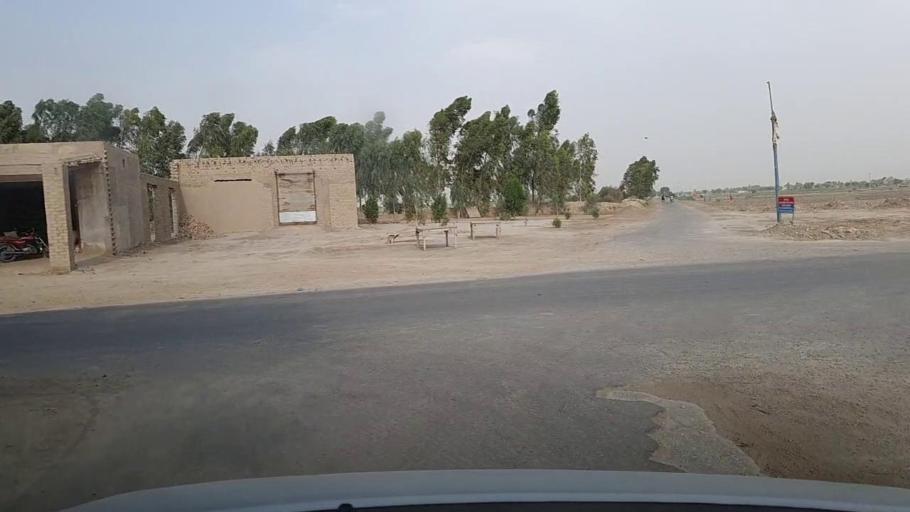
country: PK
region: Sindh
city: Dadu
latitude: 26.8111
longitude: 67.7790
